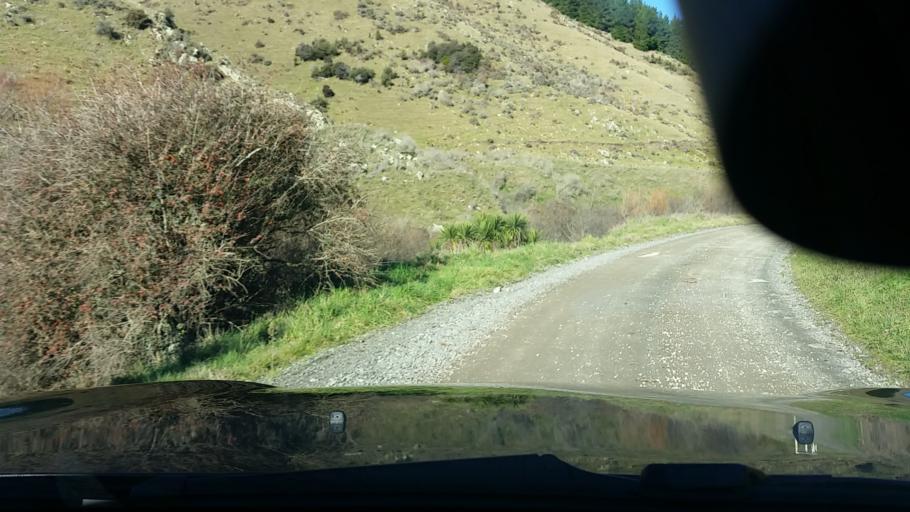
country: NZ
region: Marlborough
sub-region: Marlborough District
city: Blenheim
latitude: -41.6066
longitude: 173.9766
